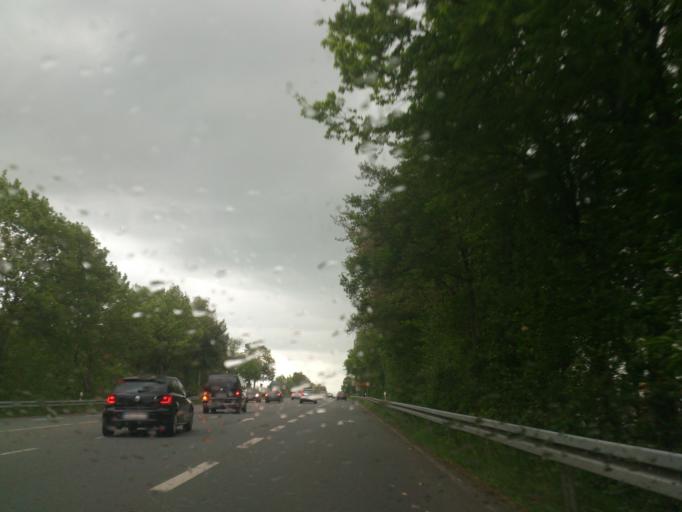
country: DE
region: North Rhine-Westphalia
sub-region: Regierungsbezirk Detmold
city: Paderborn
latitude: 51.7046
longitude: 8.7788
